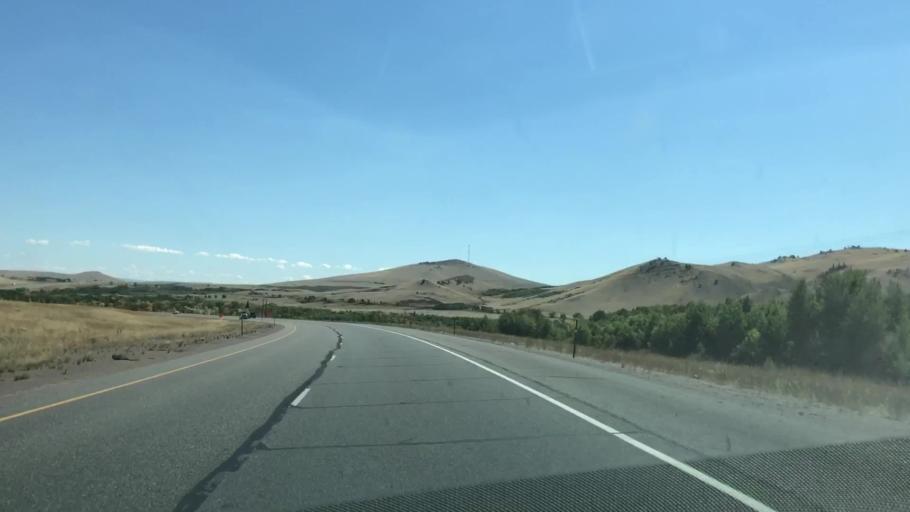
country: US
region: Wyoming
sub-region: Carbon County
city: Saratoga
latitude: 41.5988
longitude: -106.2212
